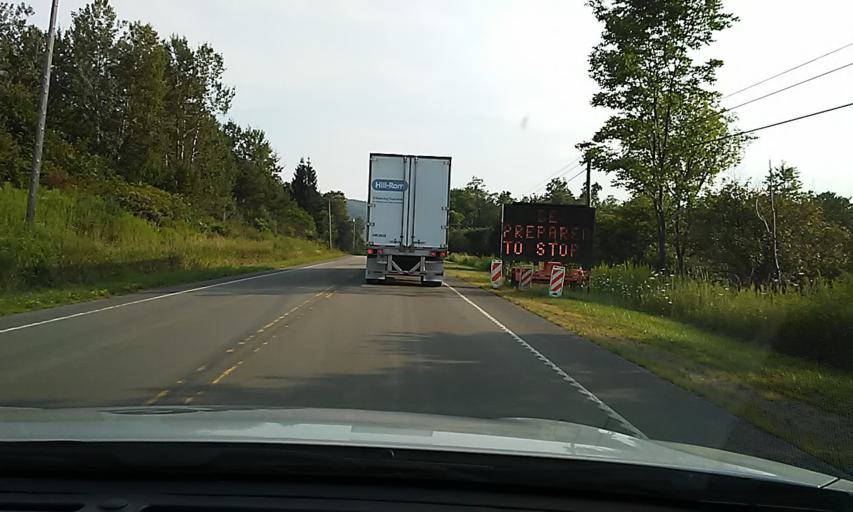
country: US
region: Pennsylvania
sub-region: McKean County
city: Smethport
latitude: 41.7570
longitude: -78.5232
